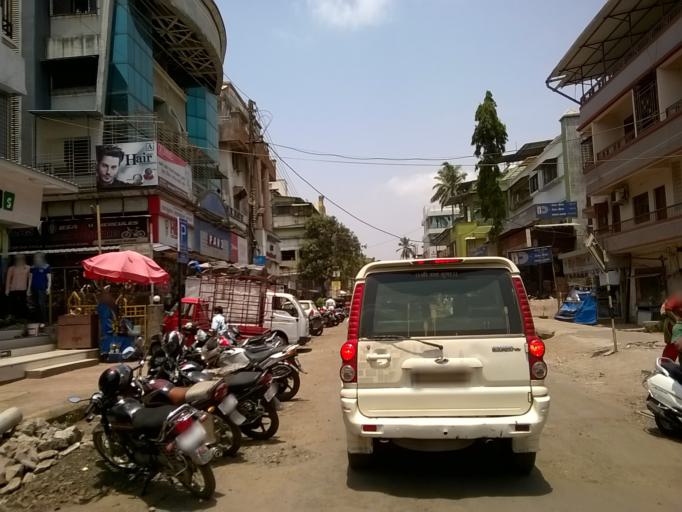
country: IN
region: Maharashtra
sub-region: Raigarh
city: Panvel
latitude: 18.9877
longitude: 73.1130
